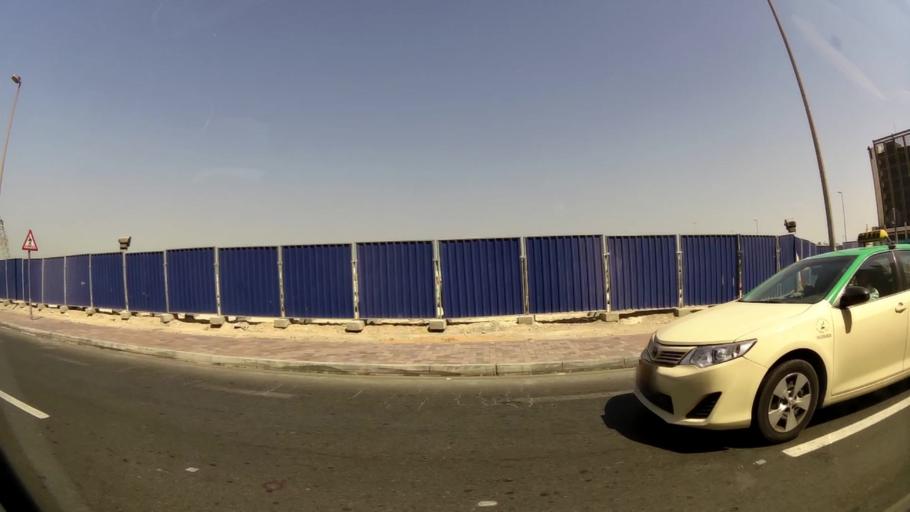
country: AE
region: Ash Shariqah
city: Sharjah
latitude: 25.2726
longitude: 55.2983
